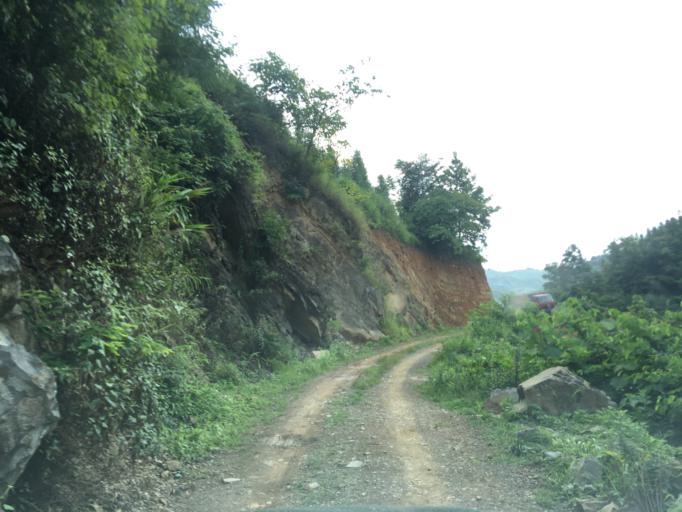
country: CN
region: Guangxi Zhuangzu Zizhiqu
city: Xinzhou
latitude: 24.8689
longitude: 105.8646
